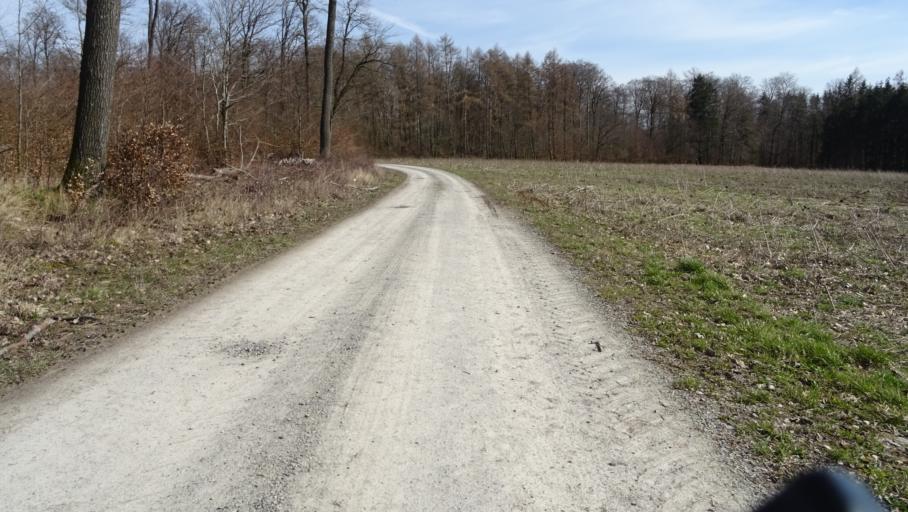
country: DE
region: Baden-Wuerttemberg
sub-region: Karlsruhe Region
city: Seckach
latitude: 49.4091
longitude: 9.3160
